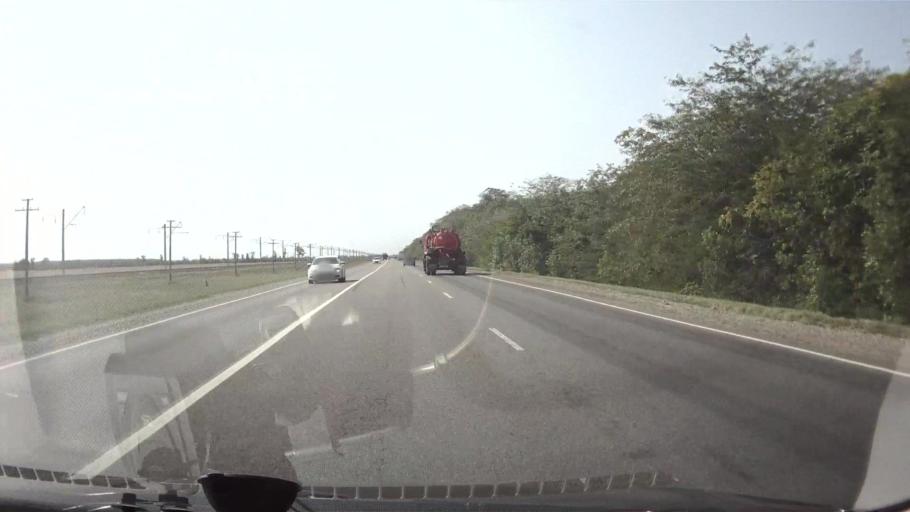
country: RU
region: Krasnodarskiy
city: Dvubratskiy
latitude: 45.2877
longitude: 39.8588
